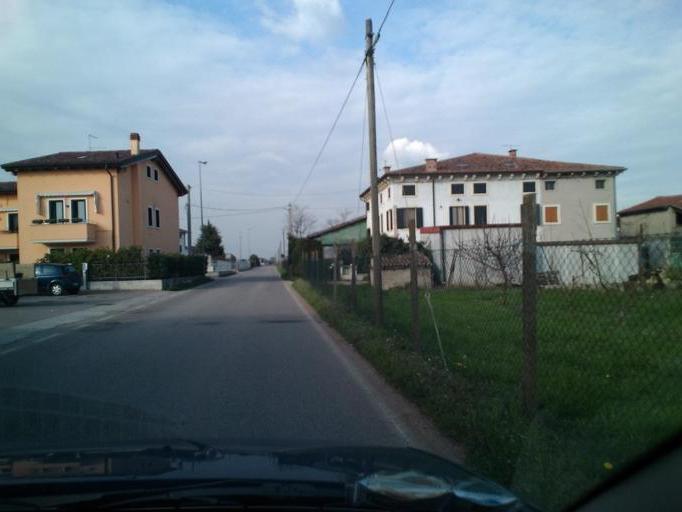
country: IT
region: Veneto
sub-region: Provincia di Verona
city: Villafranca di Verona
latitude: 45.3764
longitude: 10.8633
